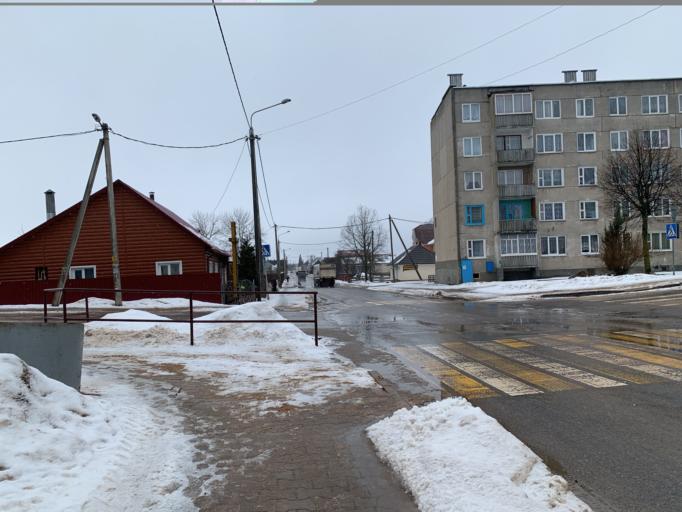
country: BY
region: Minsk
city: Nyasvizh
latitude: 53.2183
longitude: 26.6781
